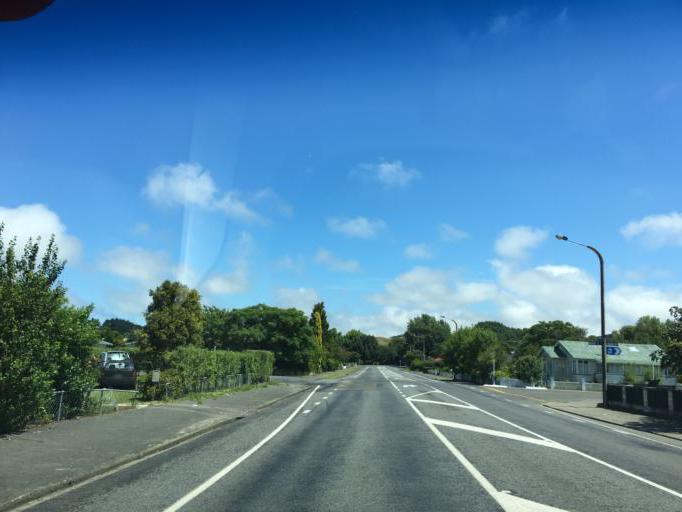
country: NZ
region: Hawke's Bay
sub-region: Wairoa District
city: Wairoa
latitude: -39.0362
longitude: 177.4168
